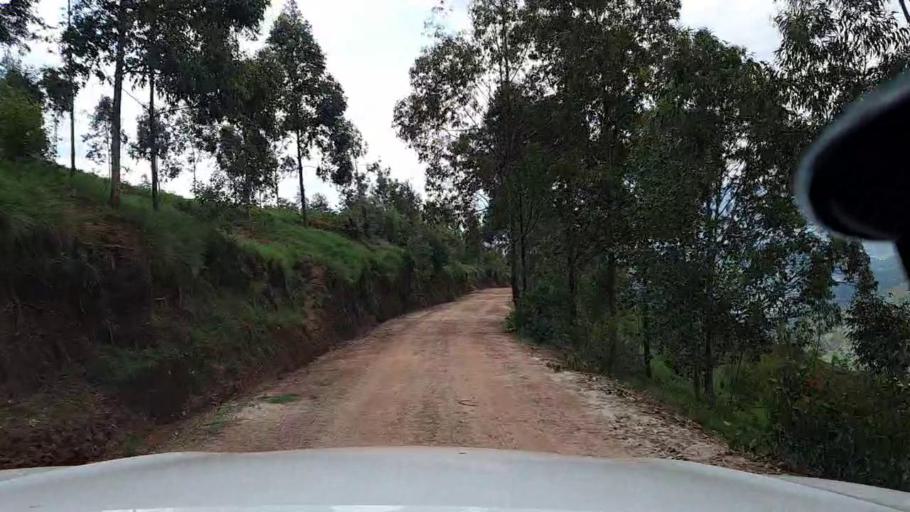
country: RW
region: Southern Province
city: Gitarama
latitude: -1.8391
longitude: 29.8262
